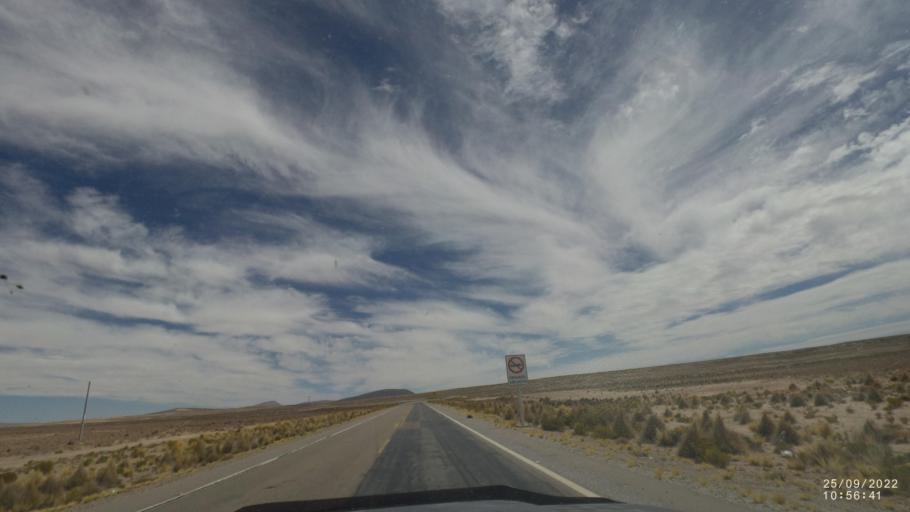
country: BO
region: Oruro
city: Challapata
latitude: -19.4821
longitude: -66.8813
